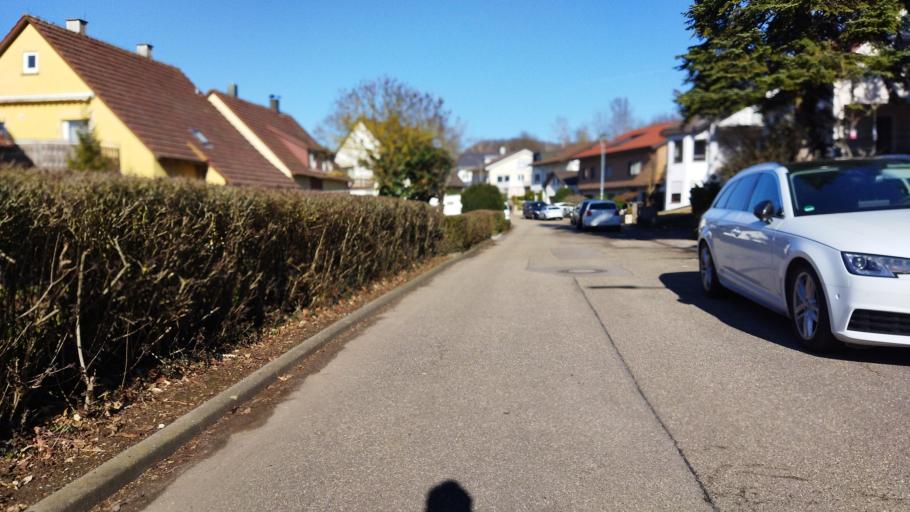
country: DE
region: Baden-Wuerttemberg
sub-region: Regierungsbezirk Stuttgart
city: Erlenbach
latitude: 49.1764
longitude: 9.2714
